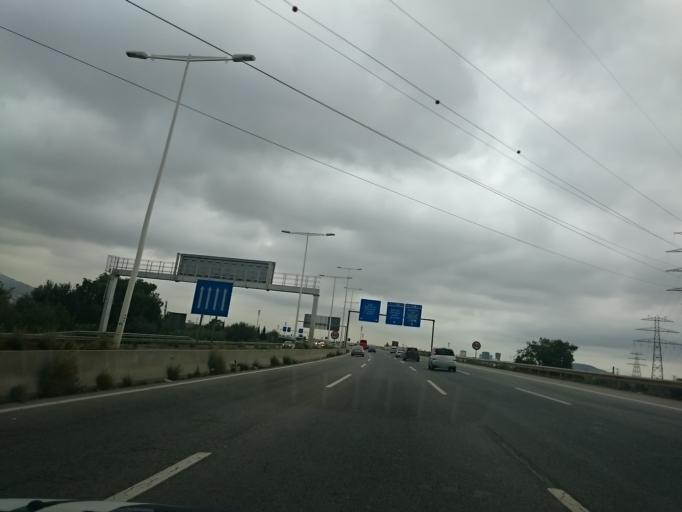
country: ES
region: Catalonia
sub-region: Provincia de Barcelona
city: Cornella de Llobregat
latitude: 41.3385
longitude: 2.0863
